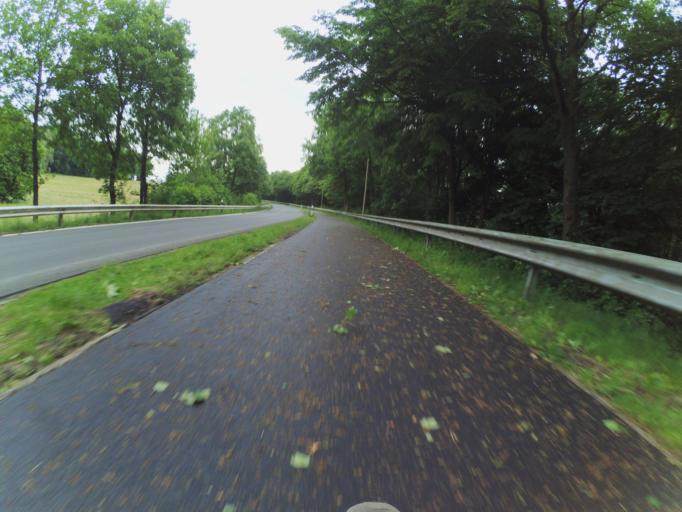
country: DE
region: North Rhine-Westphalia
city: Ibbenburen
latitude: 52.3068
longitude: 7.6681
